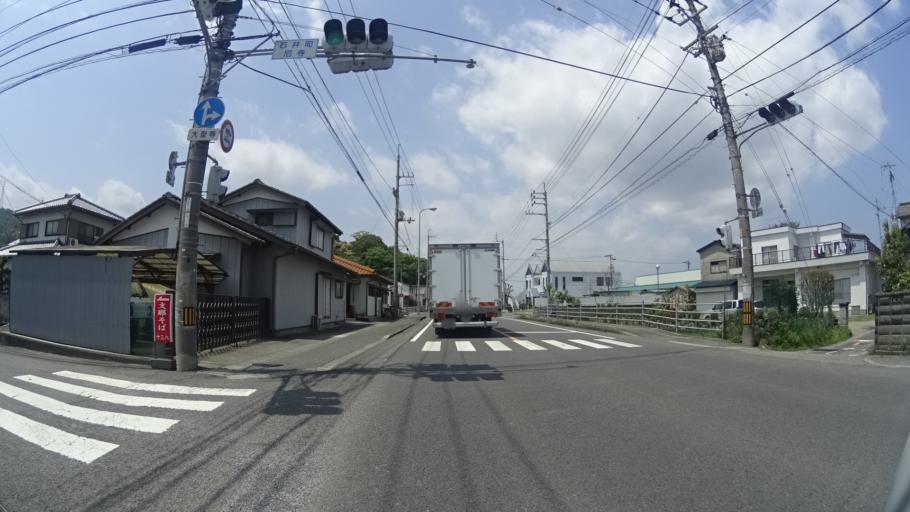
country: JP
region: Tokushima
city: Ishii
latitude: 34.0703
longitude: 134.4675
